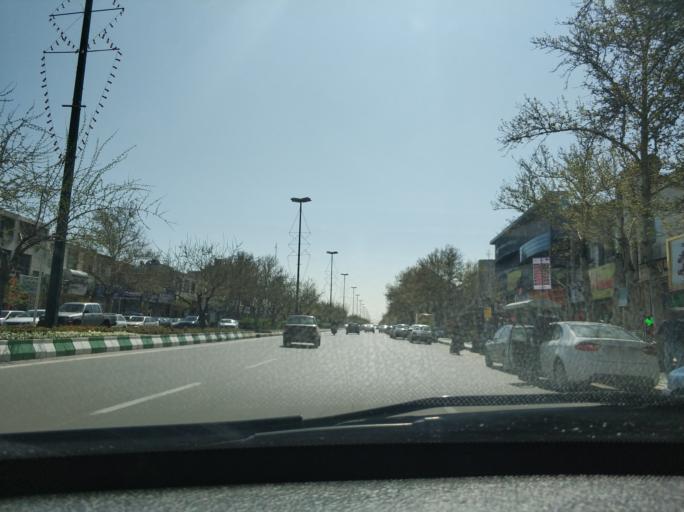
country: IR
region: Razavi Khorasan
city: Mashhad
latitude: 36.2673
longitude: 59.5993
